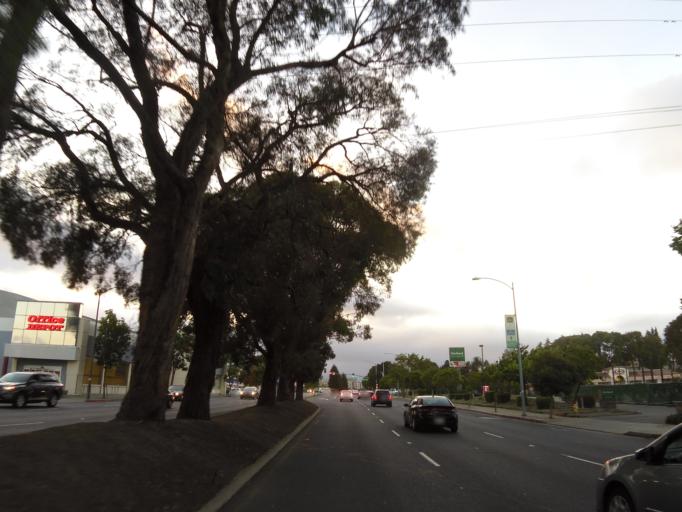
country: US
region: California
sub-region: San Mateo County
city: Millbrae
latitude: 37.6049
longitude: -122.3954
